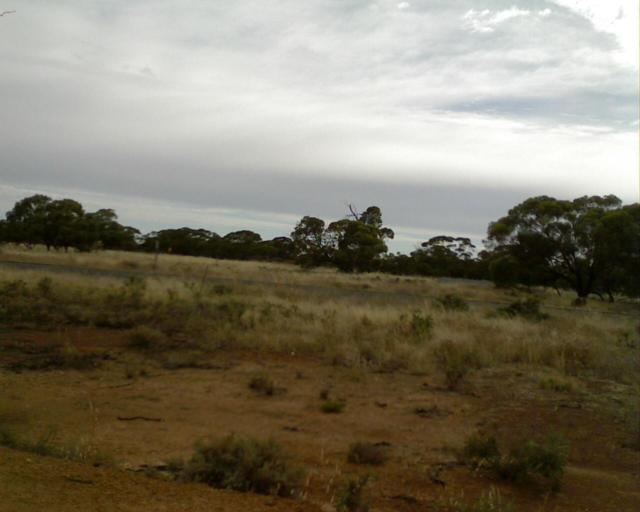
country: AU
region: Western Australia
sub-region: Moora
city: Moora
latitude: -29.7728
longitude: 115.9283
